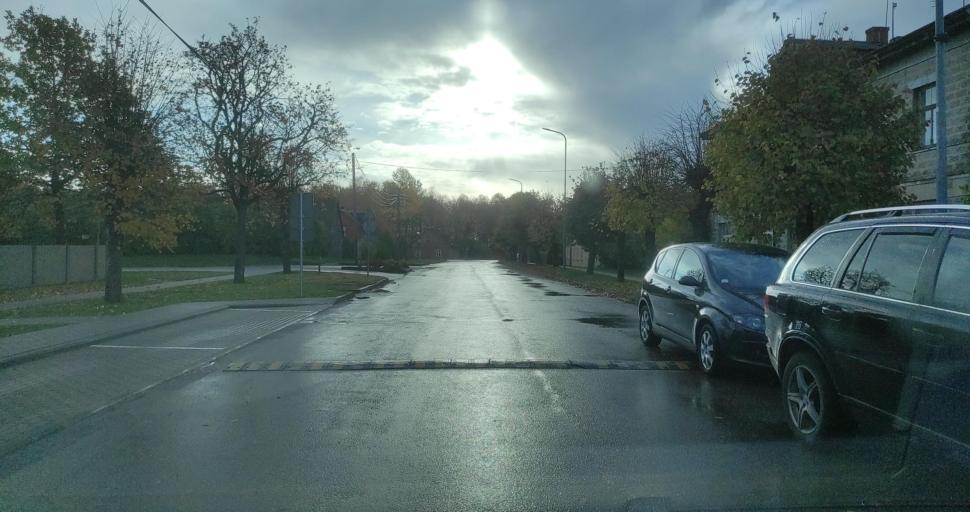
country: LV
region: Skrunda
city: Skrunda
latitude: 56.6748
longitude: 22.0215
